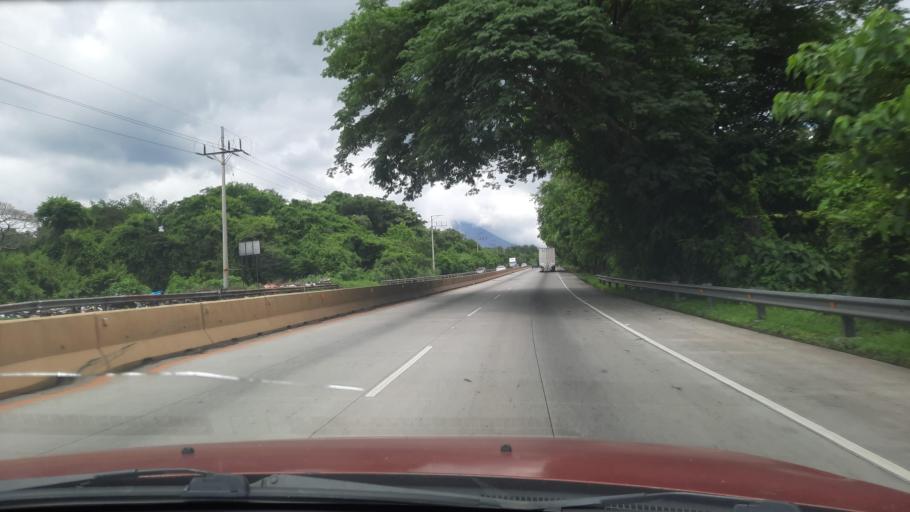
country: SV
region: Sonsonate
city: Sonzacate
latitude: 13.7363
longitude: -89.6987
